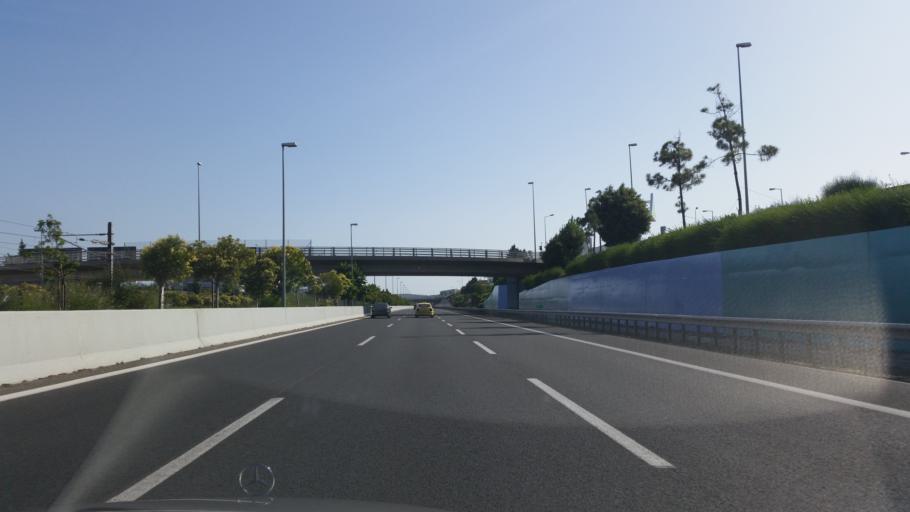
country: GR
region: Attica
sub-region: Nomarchia Anatolikis Attikis
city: Spata
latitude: 37.9283
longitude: 23.9360
